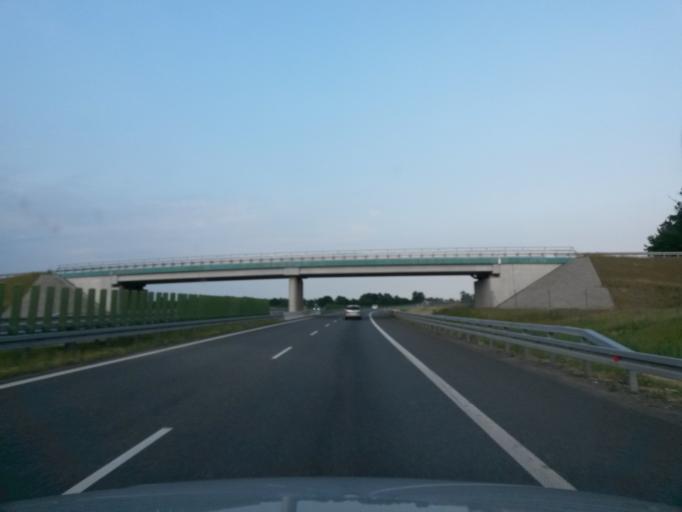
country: PL
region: Lower Silesian Voivodeship
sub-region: Powiat olesnicki
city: Miedzyborz
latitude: 51.3053
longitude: 17.6067
